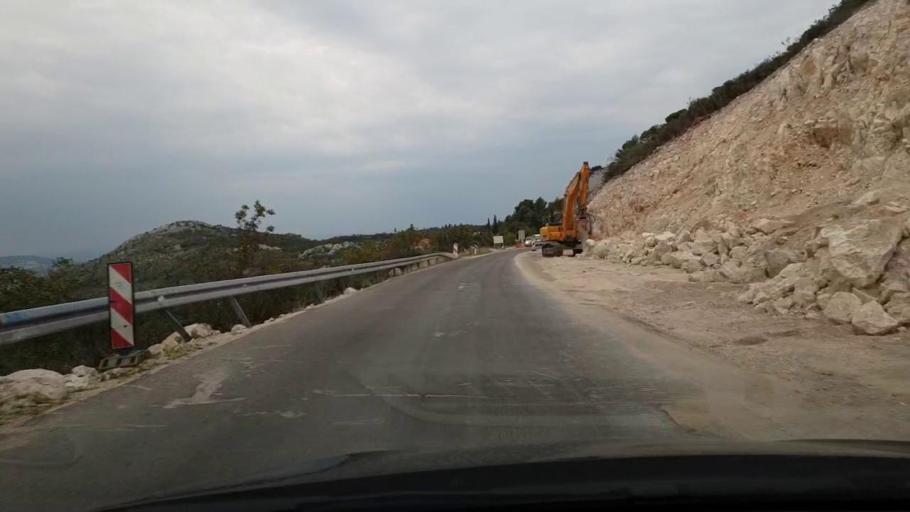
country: HR
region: Dubrovacko-Neretvanska
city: Cibaca
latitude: 42.6502
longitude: 18.1594
